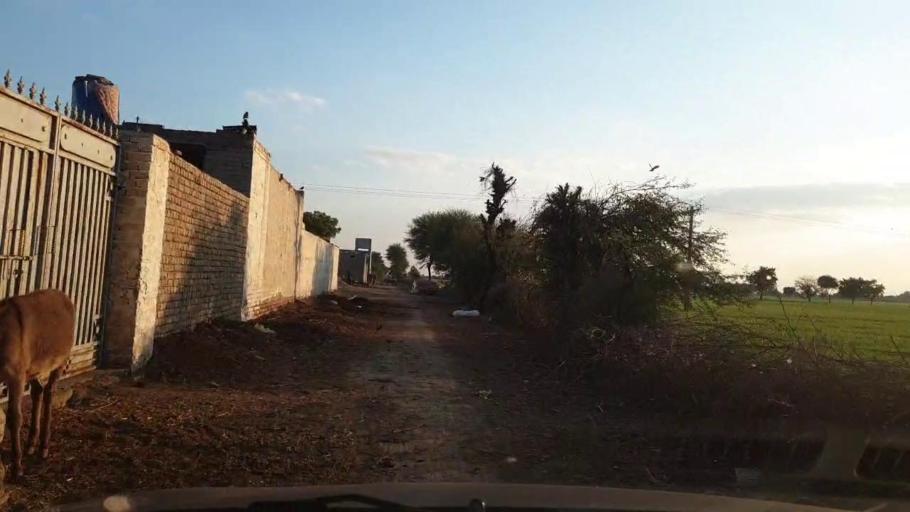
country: PK
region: Sindh
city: Sinjhoro
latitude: 25.9962
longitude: 68.8014
